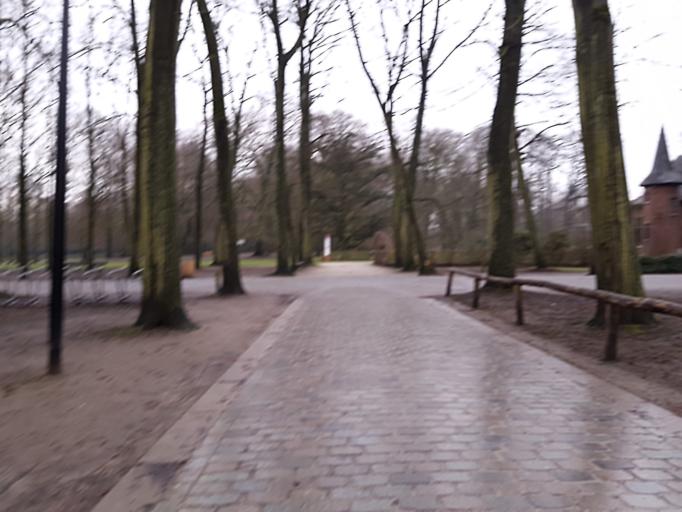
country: BE
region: Flanders
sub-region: Provincie Antwerpen
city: Borsbeek
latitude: 51.2183
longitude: 4.4666
